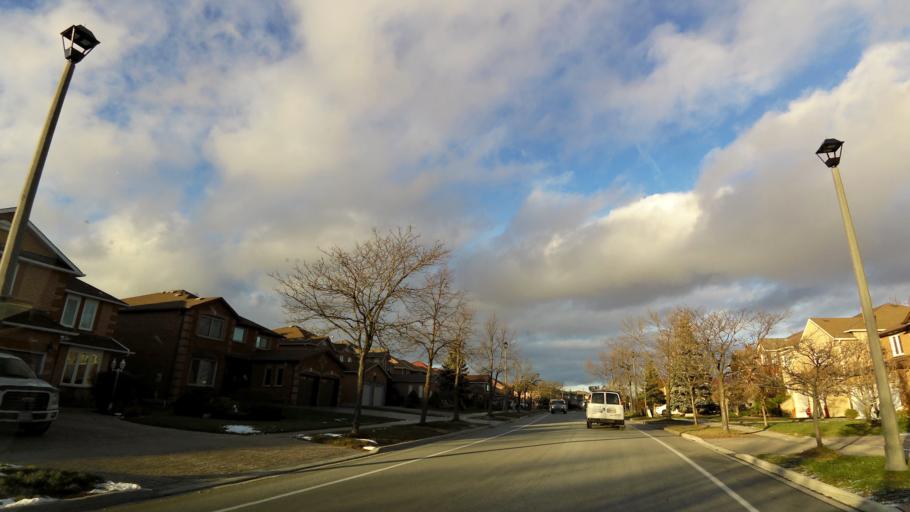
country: CA
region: Ontario
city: Mississauga
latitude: 43.6101
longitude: -79.7087
